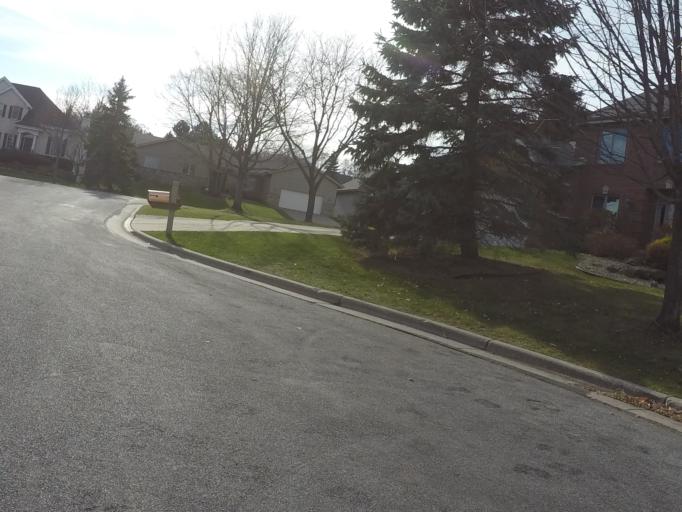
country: US
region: Wisconsin
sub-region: Dane County
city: Middleton
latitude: 43.0785
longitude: -89.5394
